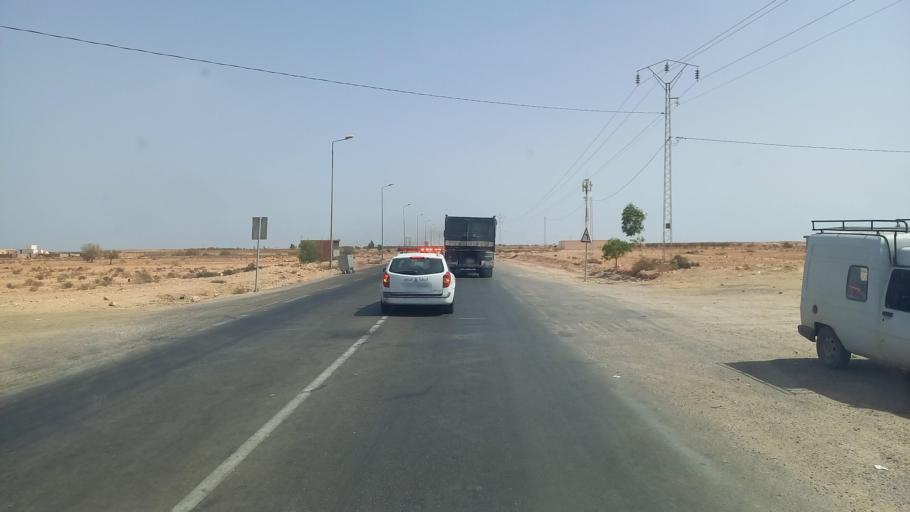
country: TN
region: Madanin
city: Medenine
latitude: 33.3747
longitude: 10.6943
